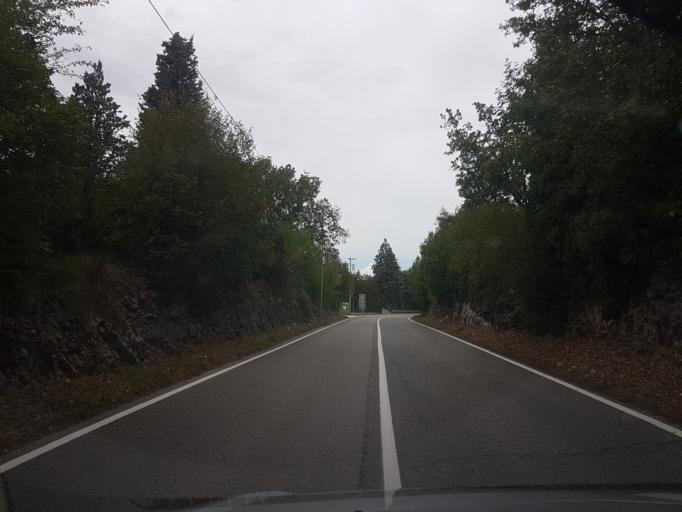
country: IT
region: Friuli Venezia Giulia
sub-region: Provincia di Trieste
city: Aurisina
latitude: 45.7549
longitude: 13.6899
